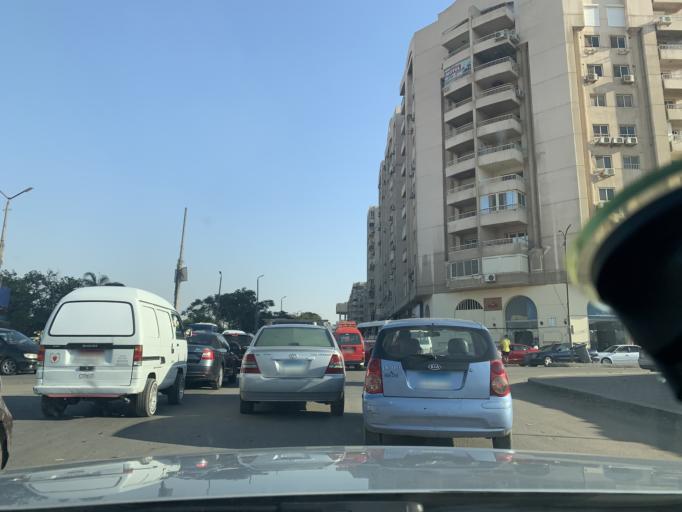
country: EG
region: Muhafazat al Qahirah
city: Cairo
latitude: 30.0389
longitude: 31.3462
